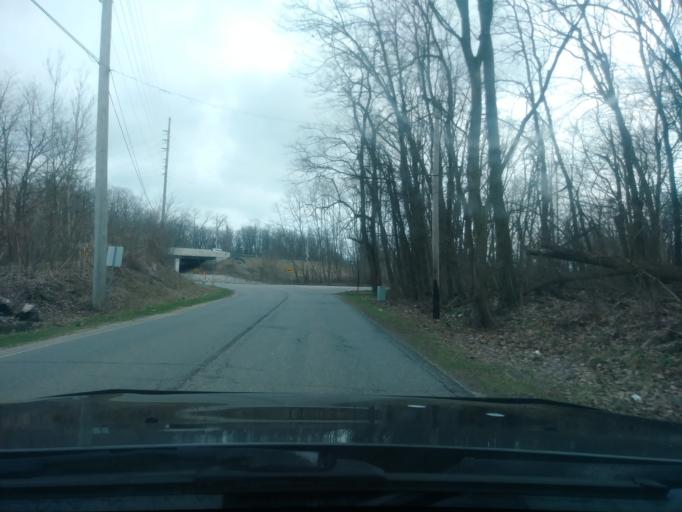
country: US
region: Indiana
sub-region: LaPorte County
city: LaPorte
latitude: 41.6304
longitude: -86.7966
